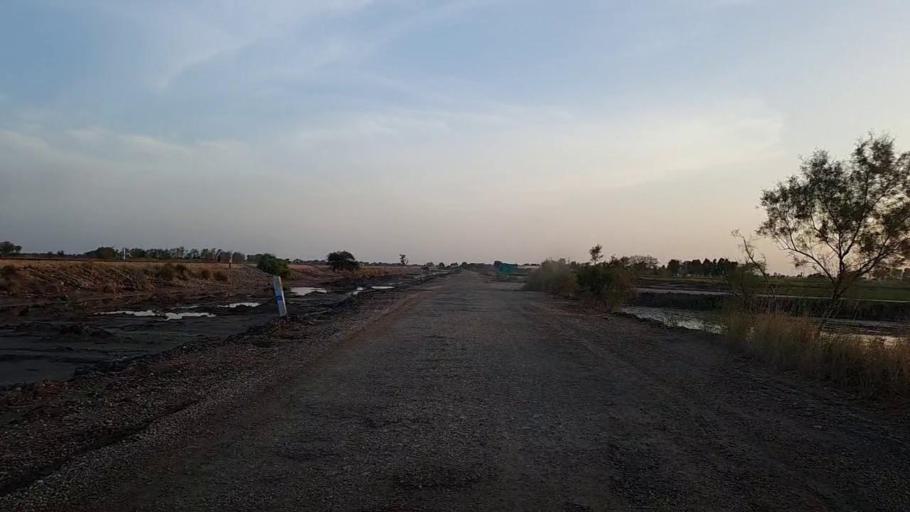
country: PK
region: Sindh
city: Karaundi
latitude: 27.0518
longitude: 68.3875
